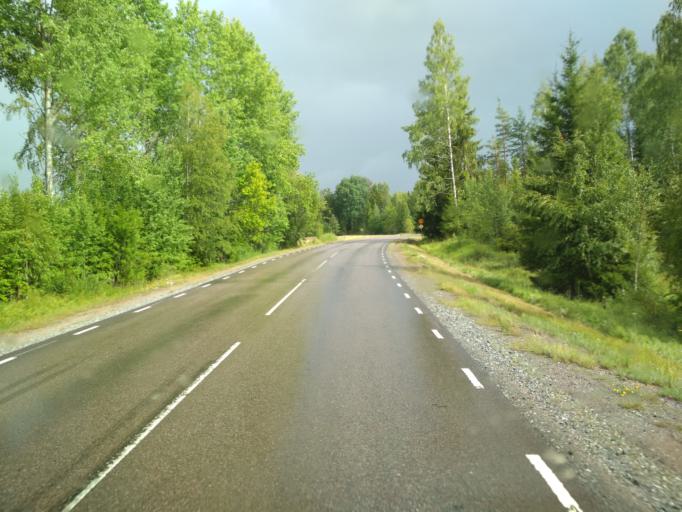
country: SE
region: Vaestmanland
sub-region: Surahammars Kommun
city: Ramnas
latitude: 59.8822
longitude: 16.0686
